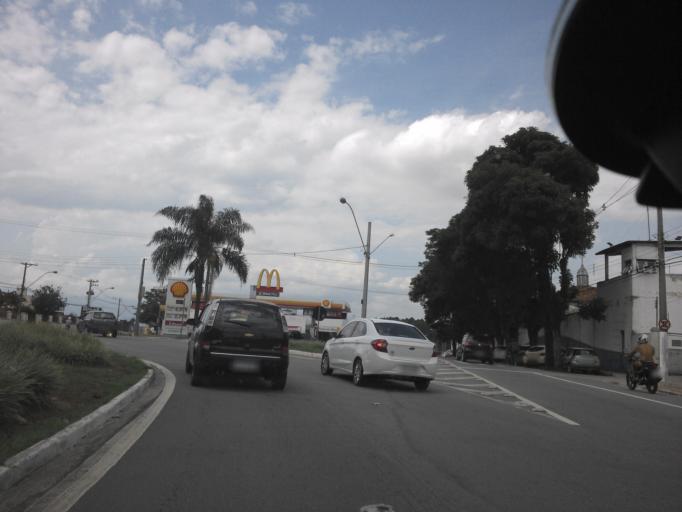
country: BR
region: Sao Paulo
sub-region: Taubate
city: Taubate
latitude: -23.0138
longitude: -45.5504
